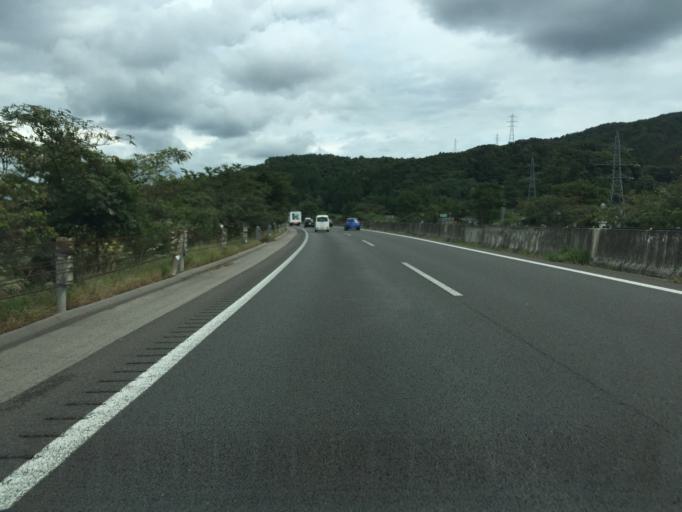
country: JP
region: Fukushima
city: Yanagawamachi-saiwaicho
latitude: 37.9231
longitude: 140.6089
